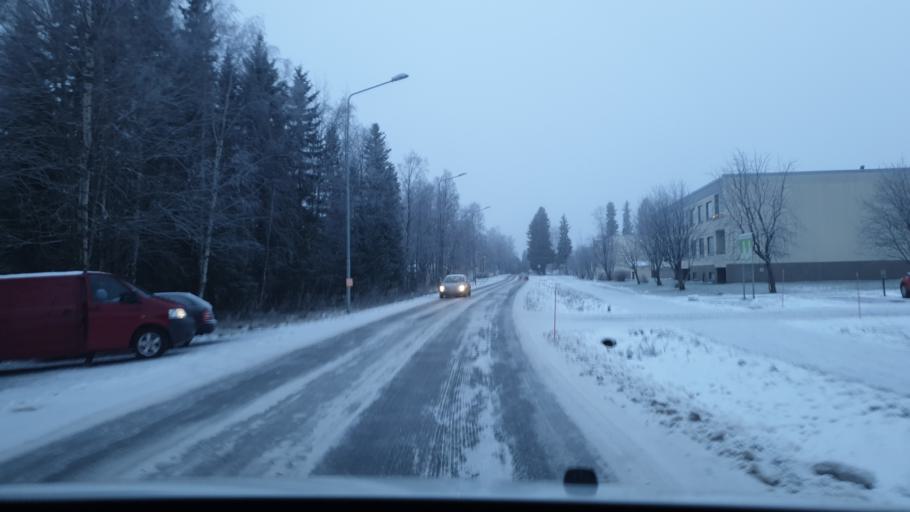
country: FI
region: Lapland
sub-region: Kemi-Tornio
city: Kemi
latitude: 65.7330
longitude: 24.6059
